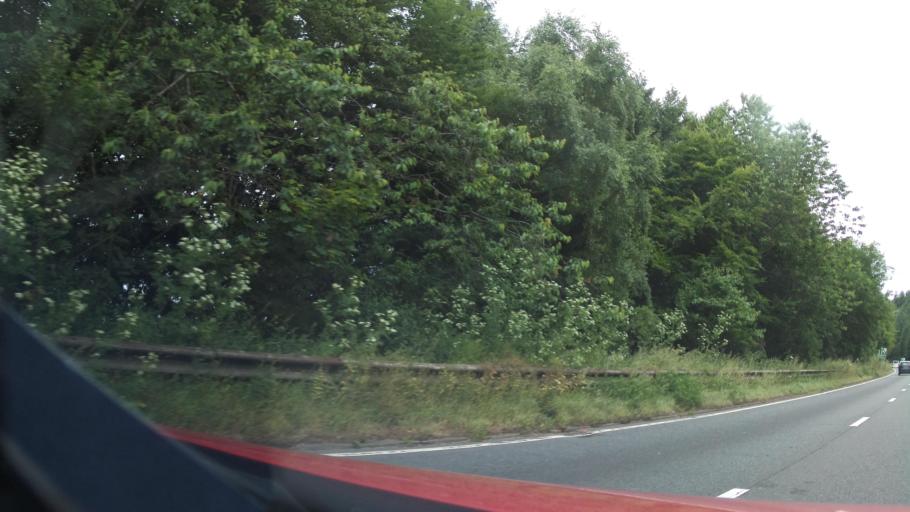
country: GB
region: England
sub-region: Devon
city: Exminster
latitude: 50.6477
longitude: -3.5419
